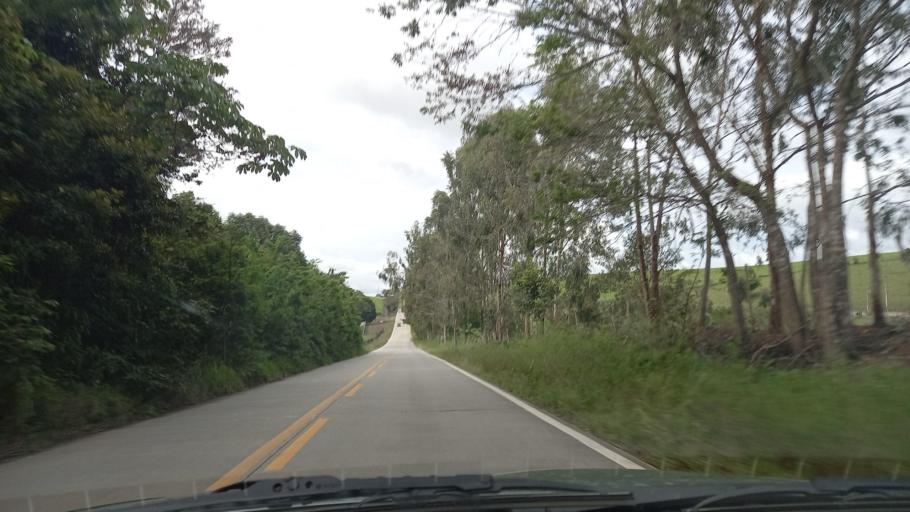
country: BR
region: Pernambuco
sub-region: Quipapa
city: Quipapa
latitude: -8.7797
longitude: -35.9342
